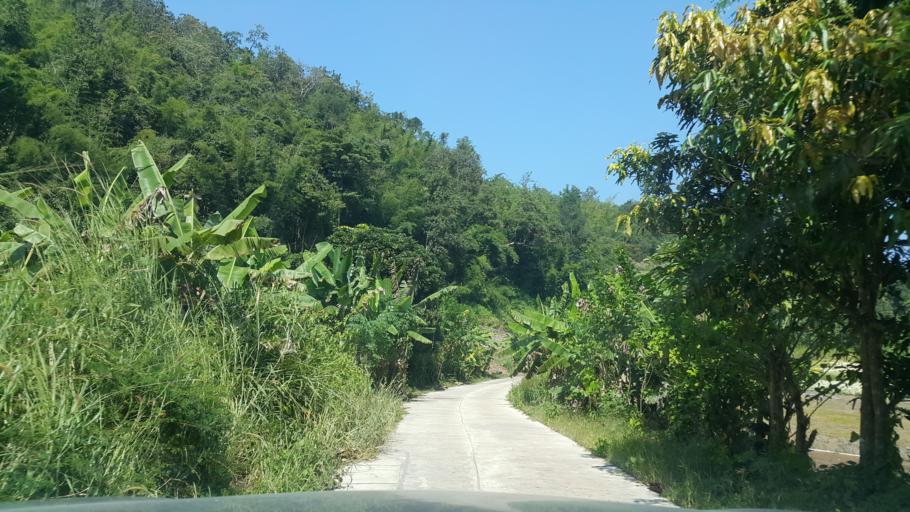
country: TH
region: Chiang Mai
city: Samoeng
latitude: 18.9177
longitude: 98.6071
